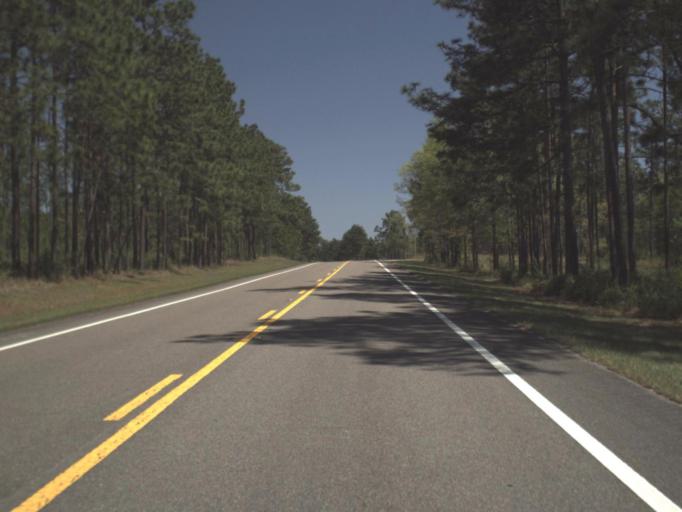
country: US
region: Florida
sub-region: Okaloosa County
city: Crestview
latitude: 30.8514
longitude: -86.8090
